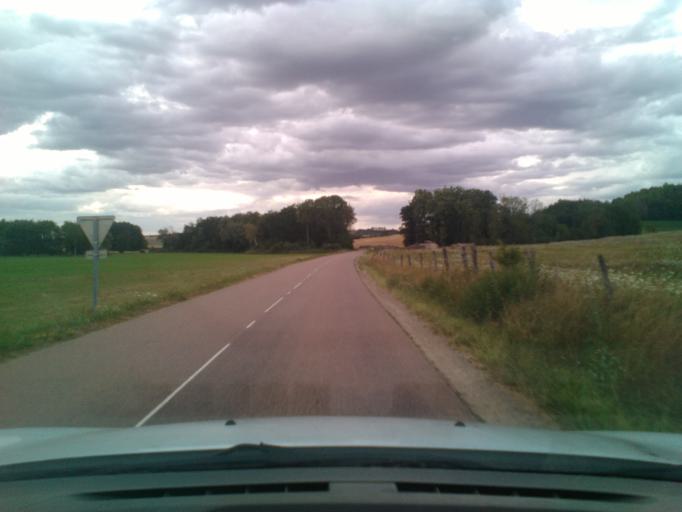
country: FR
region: Lorraine
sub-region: Departement des Vosges
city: Charmes
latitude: 48.3483
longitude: 6.2769
